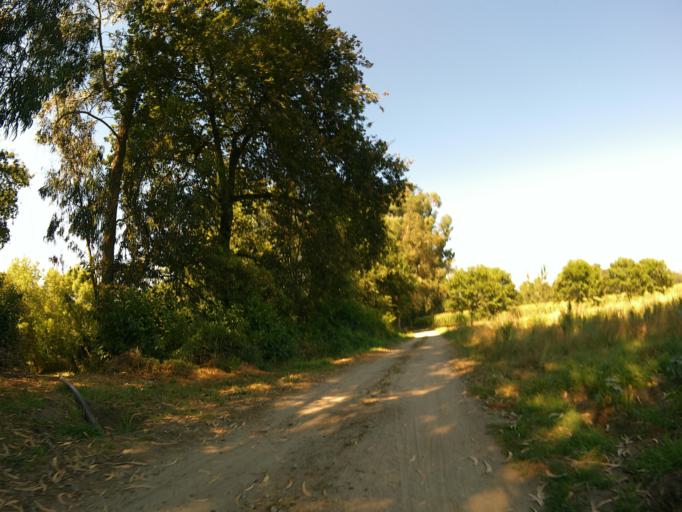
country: PT
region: Viana do Castelo
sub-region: Ponte de Lima
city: Ponte de Lima
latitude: 41.7565
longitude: -8.6227
